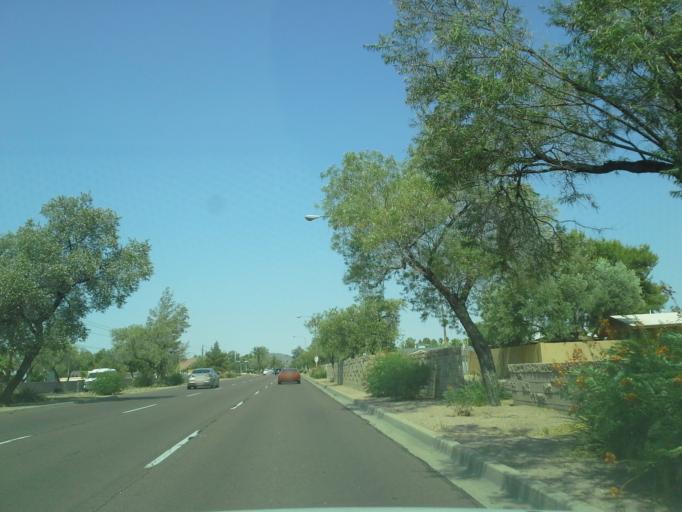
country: US
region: Arizona
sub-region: Maricopa County
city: Paradise Valley
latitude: 33.5971
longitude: -112.0178
